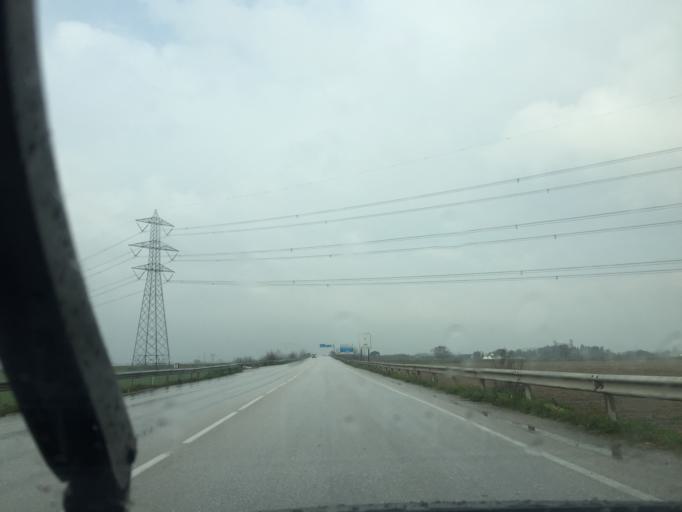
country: IT
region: Apulia
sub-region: Provincia di Foggia
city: Foggia
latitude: 41.4981
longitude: 15.5272
